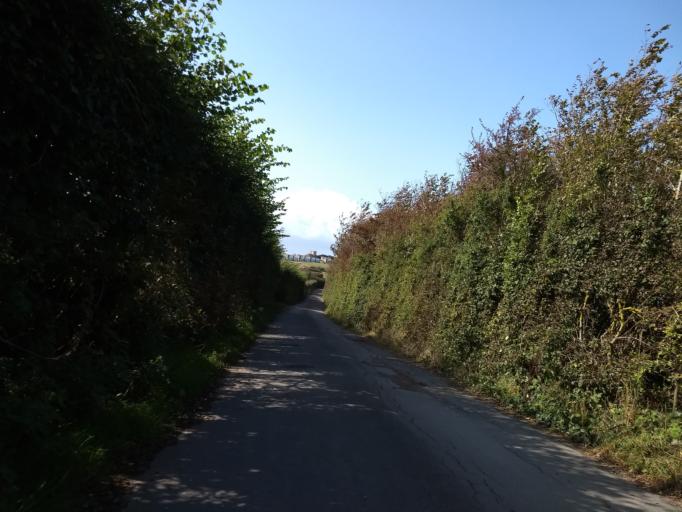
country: GB
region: England
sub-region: Isle of Wight
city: Totland
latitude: 50.6958
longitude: -1.5278
